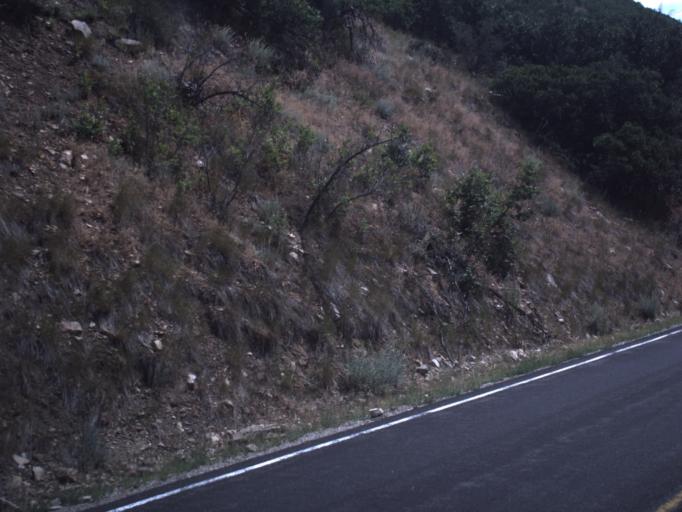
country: US
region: Utah
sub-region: Summit County
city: Francis
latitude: 40.5670
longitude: -111.1923
